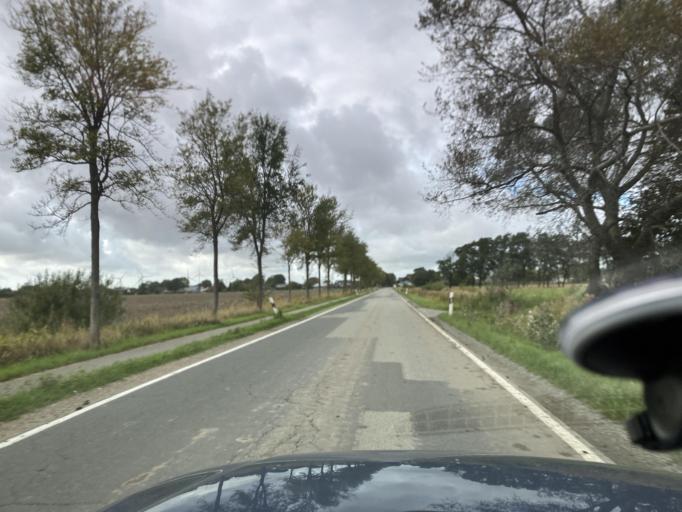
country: DE
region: Schleswig-Holstein
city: Neuenkirchen
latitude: 54.2345
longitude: 9.0079
